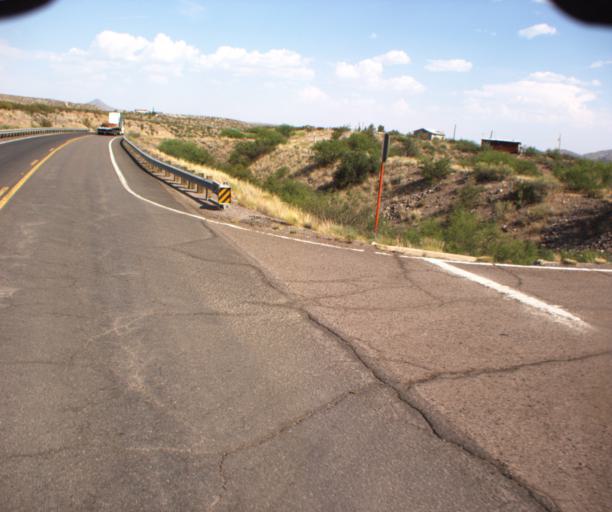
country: US
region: Arizona
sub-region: Greenlee County
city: Clifton
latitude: 32.9382
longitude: -109.2177
